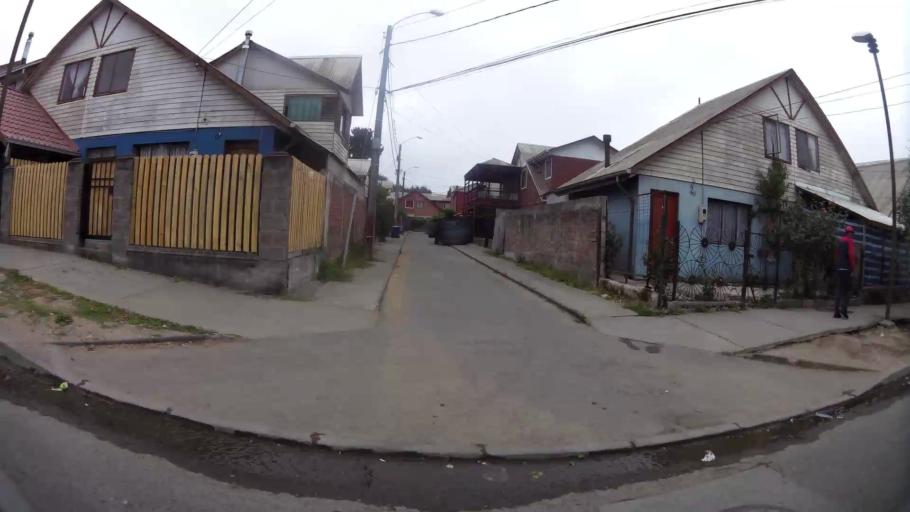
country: CL
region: Biobio
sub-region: Provincia de Concepcion
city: Concepcion
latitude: -36.8195
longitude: -72.9862
